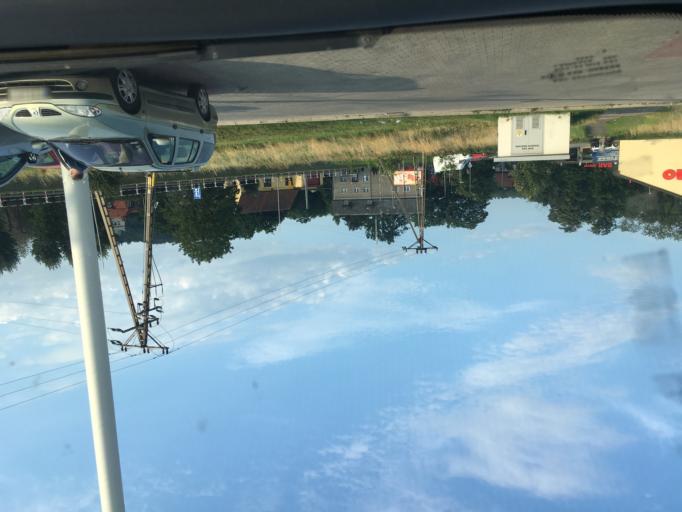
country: PL
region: Lower Silesian Voivodeship
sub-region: Powiat zabkowicki
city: Zloty Stok
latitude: 50.4461
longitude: 16.8726
